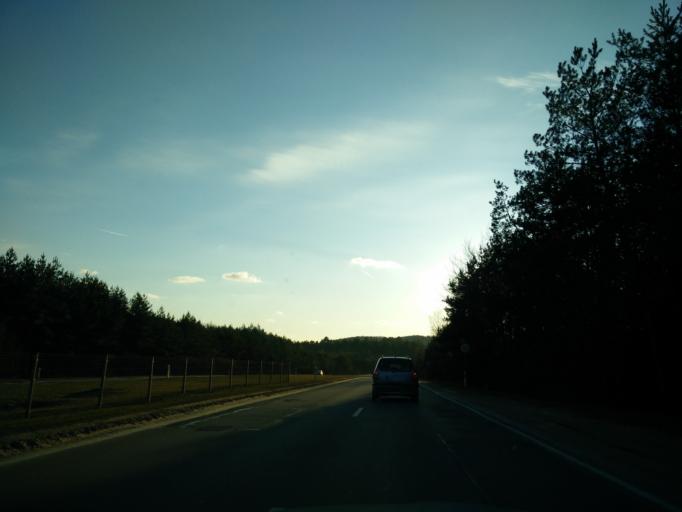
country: LT
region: Vilnius County
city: Rasos
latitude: 54.6931
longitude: 25.3778
